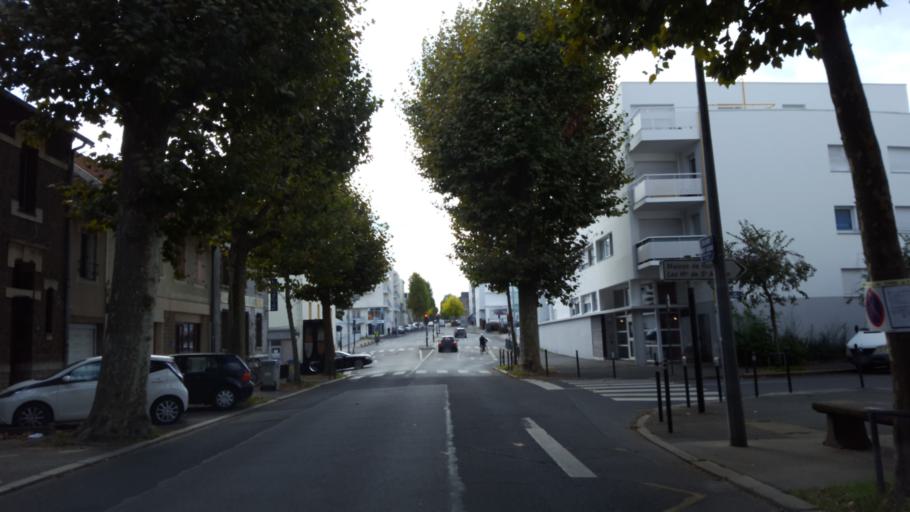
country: FR
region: Pays de la Loire
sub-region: Departement de la Loire-Atlantique
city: Nantes
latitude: 47.2078
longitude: -1.5787
